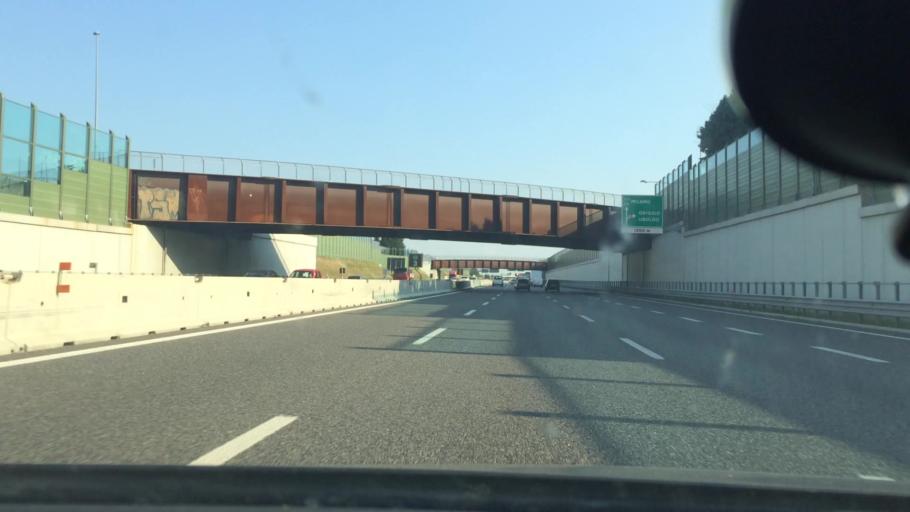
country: IT
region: Lombardy
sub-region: Provincia di Varese
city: Uboldo
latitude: 45.6201
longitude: 9.0132
